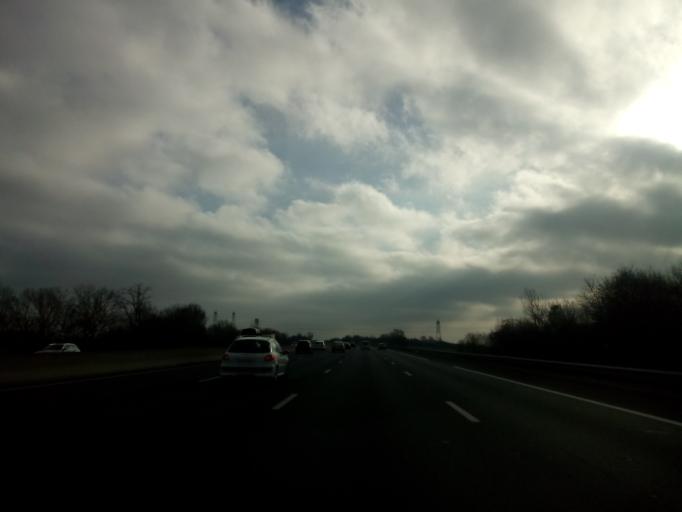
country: FR
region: Rhone-Alpes
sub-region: Departement du Rhone
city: Saint-Bonnet-de-Mure
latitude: 45.6921
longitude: 4.9865
